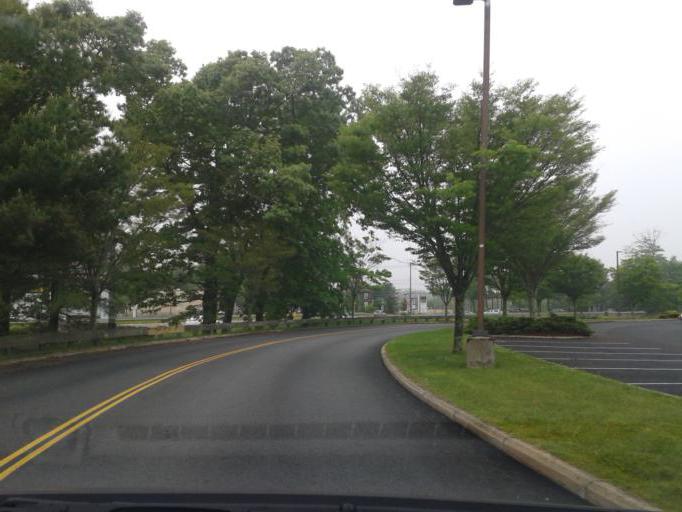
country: US
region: Massachusetts
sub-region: Bristol County
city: Smith Mills
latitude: 41.6407
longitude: -70.9952
